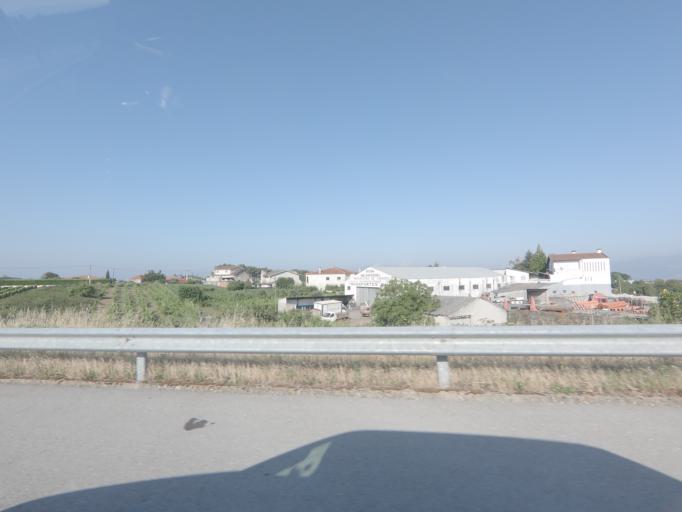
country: PT
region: Vila Real
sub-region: Vila Real
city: Vila Real
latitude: 41.2784
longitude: -7.6907
